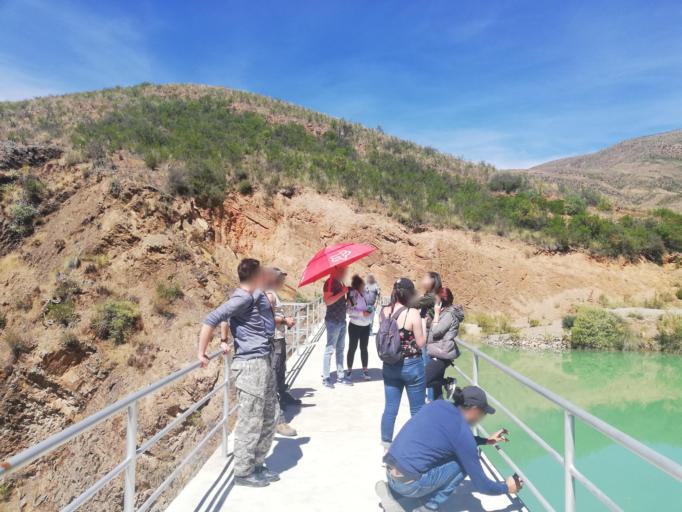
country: BO
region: Cochabamba
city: Tarata
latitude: -17.6363
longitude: -66.1146
